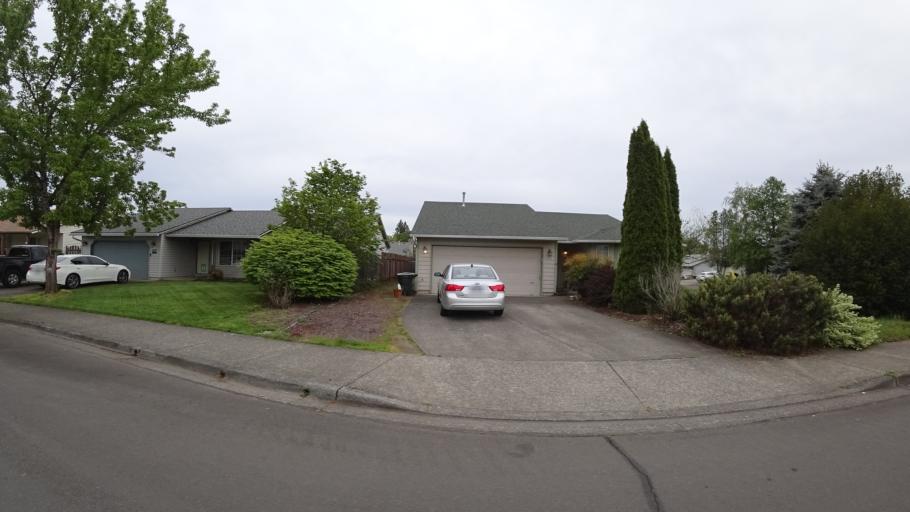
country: US
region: Oregon
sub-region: Washington County
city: Aloha
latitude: 45.5115
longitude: -122.9102
